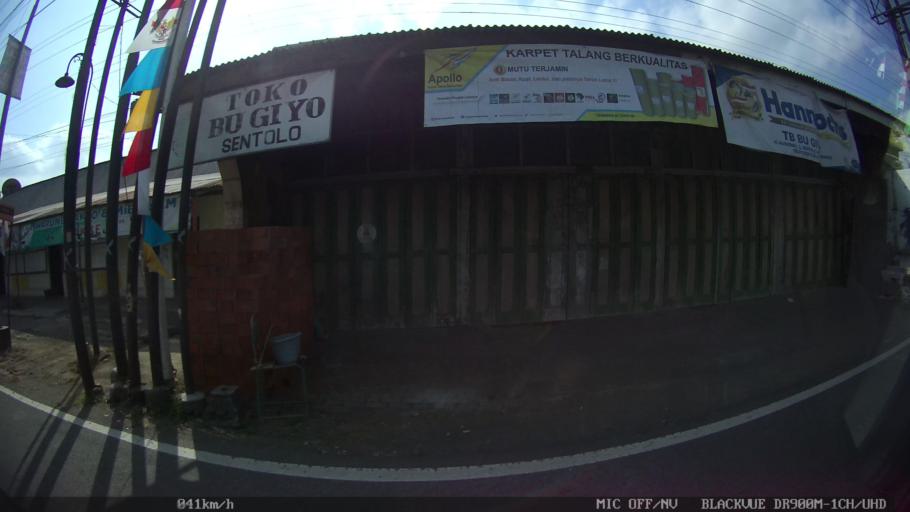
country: ID
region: Daerah Istimewa Yogyakarta
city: Godean
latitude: -7.8346
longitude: 110.2204
